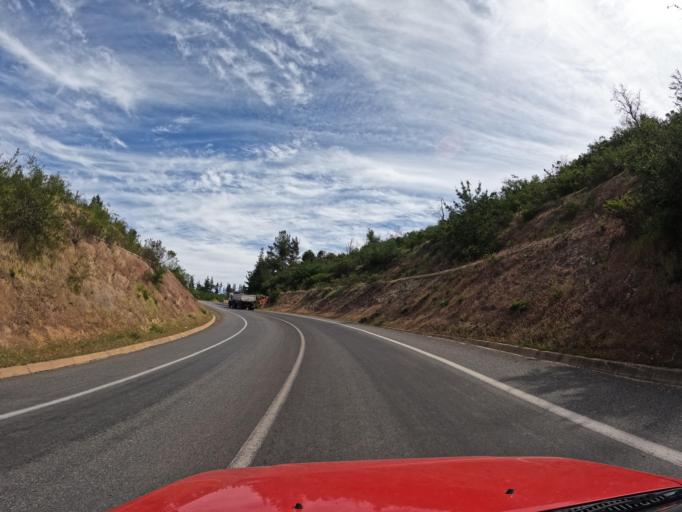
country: CL
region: Maule
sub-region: Provincia de Talca
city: Talca
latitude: -35.1642
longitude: -71.9725
